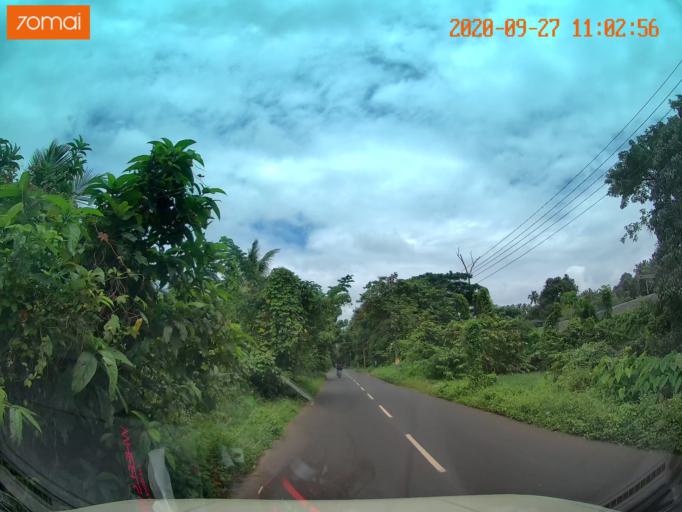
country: IN
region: Kerala
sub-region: Thrissur District
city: Irinjalakuda
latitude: 10.4197
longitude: 76.2612
